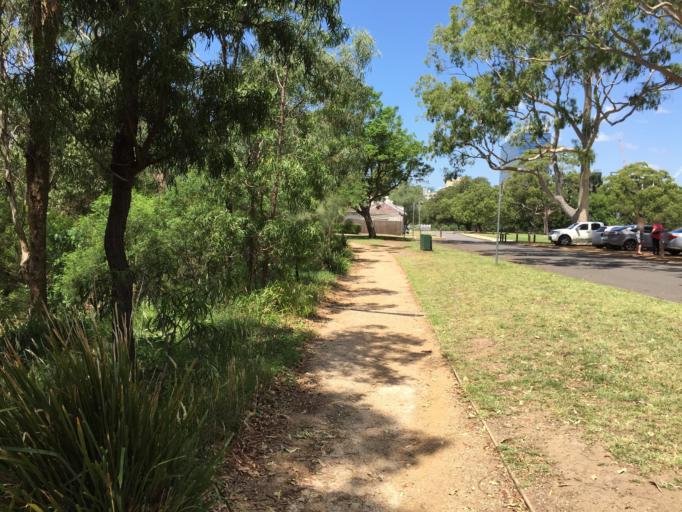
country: AU
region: New South Wales
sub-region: Parramatta
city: City of Parramatta
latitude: -33.8121
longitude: 150.9958
